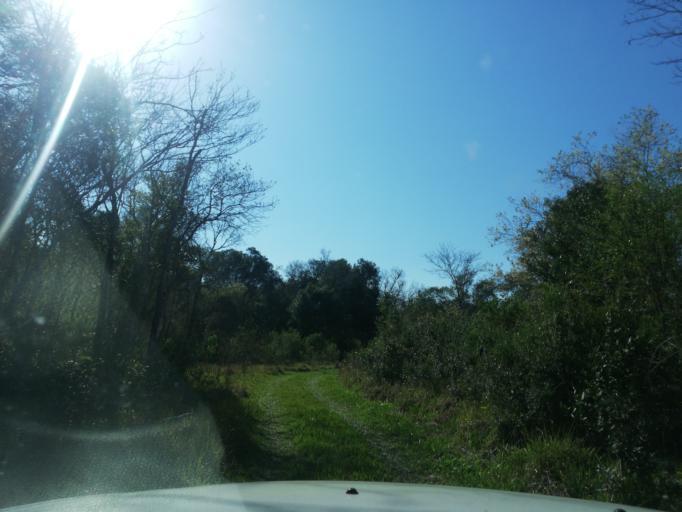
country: AR
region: Misiones
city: Arroyo del Medio
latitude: -27.6783
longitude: -55.3974
